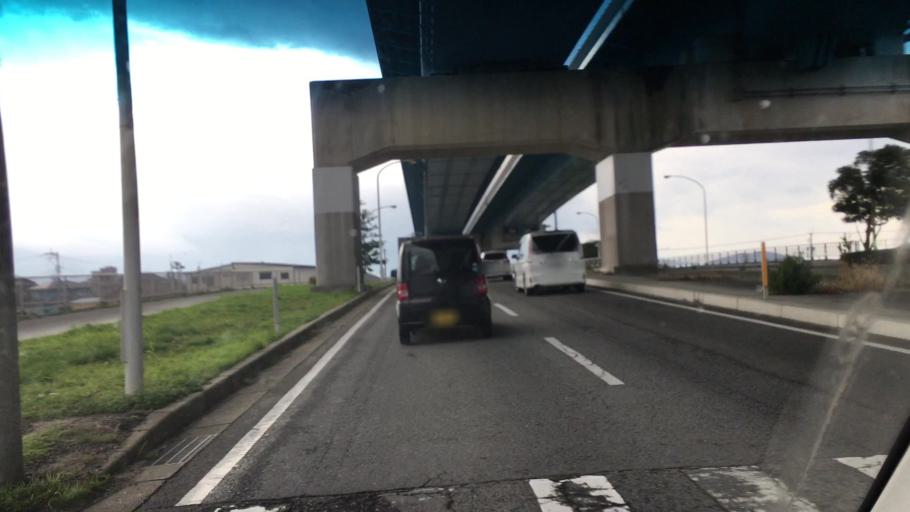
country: JP
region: Fukuoka
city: Maebaru-chuo
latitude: 33.5613
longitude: 130.2333
